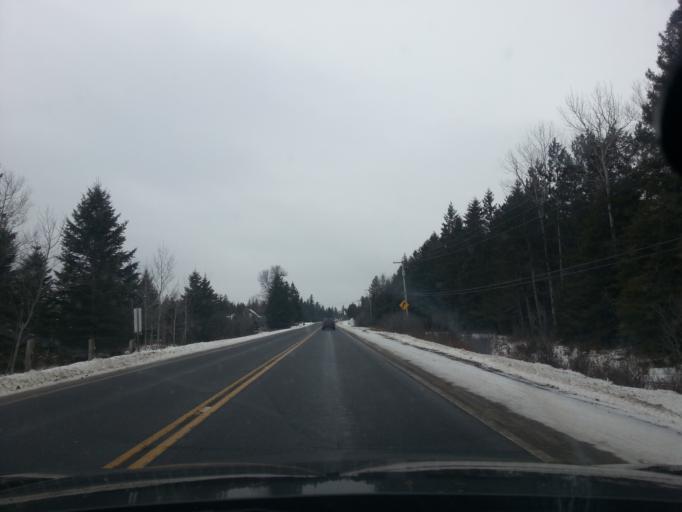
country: CA
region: Ontario
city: Carleton Place
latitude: 45.2906
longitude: -76.0929
